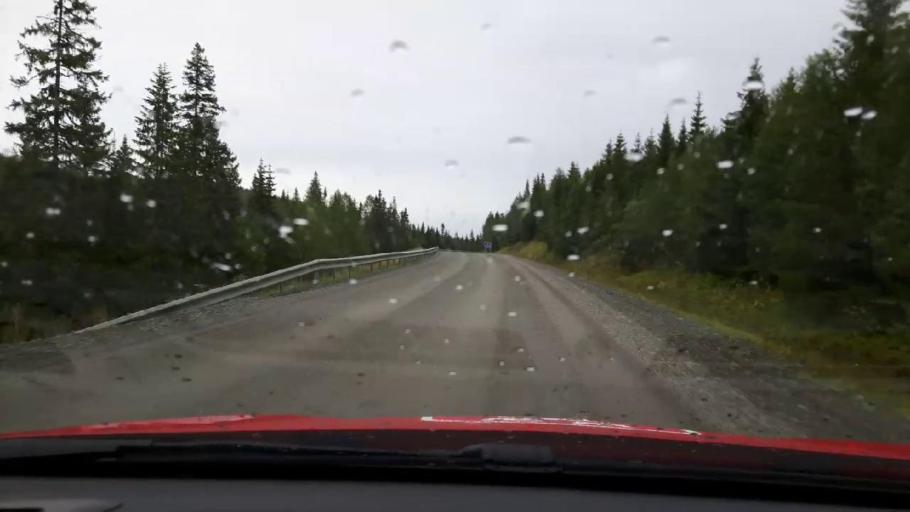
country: SE
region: Jaemtland
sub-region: Are Kommun
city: Are
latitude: 63.4365
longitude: 12.7232
